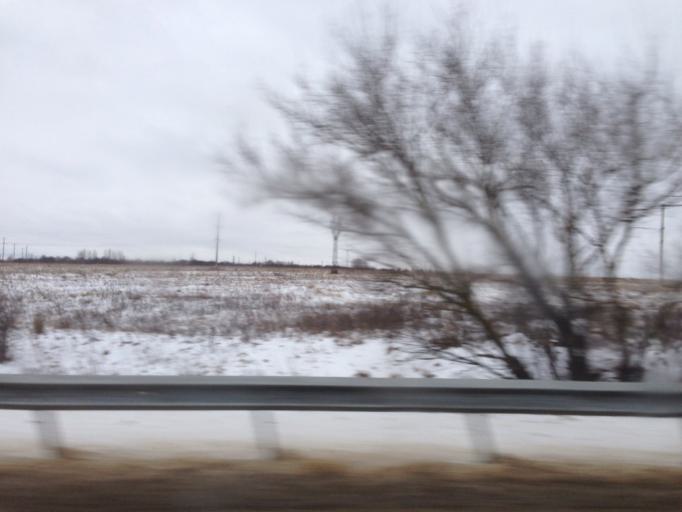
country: RU
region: Tula
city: Kamenetskiy
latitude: 53.9974
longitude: 38.2056
